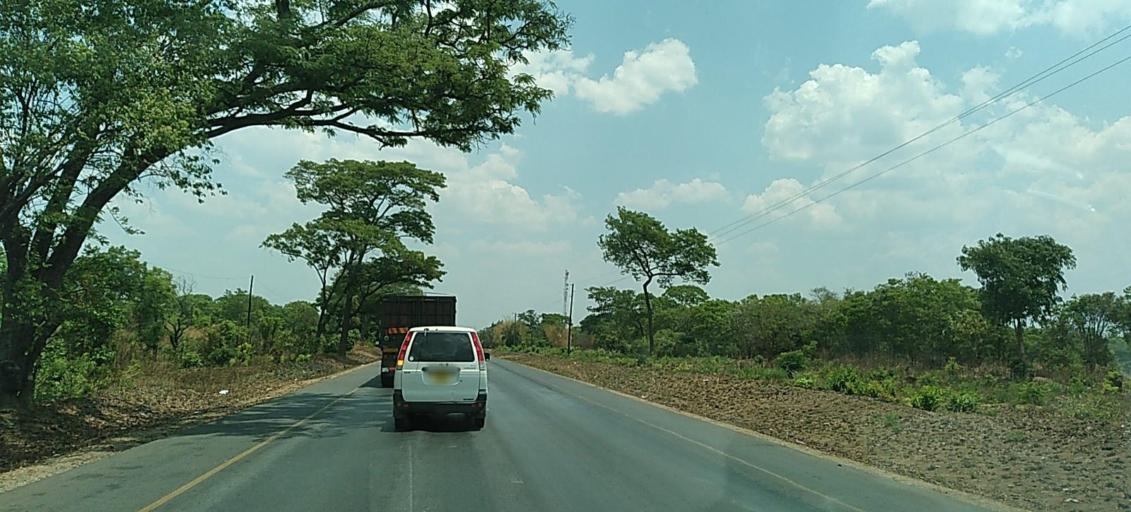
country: ZM
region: Central
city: Kapiri Mposhi
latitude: -14.2017
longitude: 28.5869
